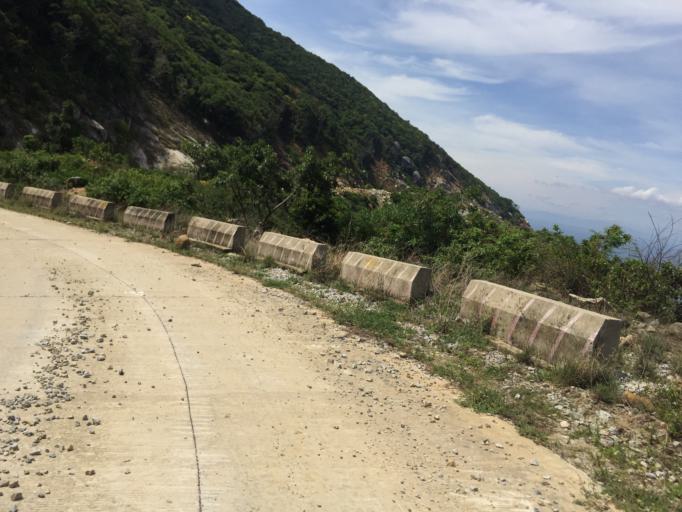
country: VN
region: Quang Nam
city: Hoi An
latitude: 15.9761
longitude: 108.5031
